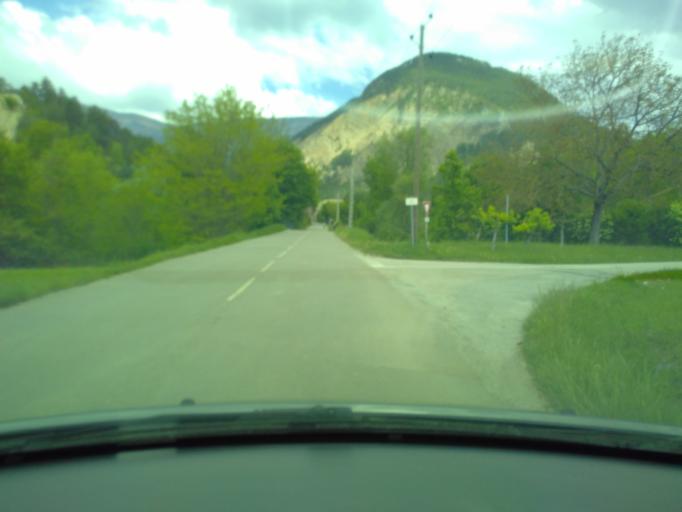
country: FR
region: Rhone-Alpes
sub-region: Departement de la Drome
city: Die
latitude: 44.6707
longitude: 5.4734
